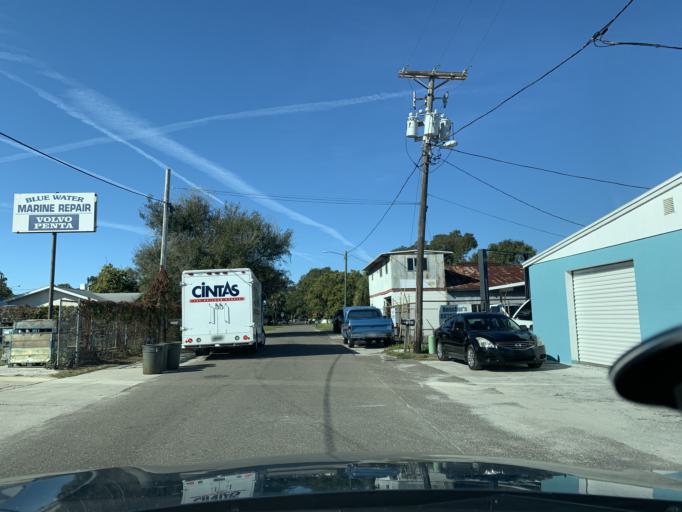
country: US
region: Florida
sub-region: Pinellas County
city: Gulfport
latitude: 27.7538
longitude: -82.7006
